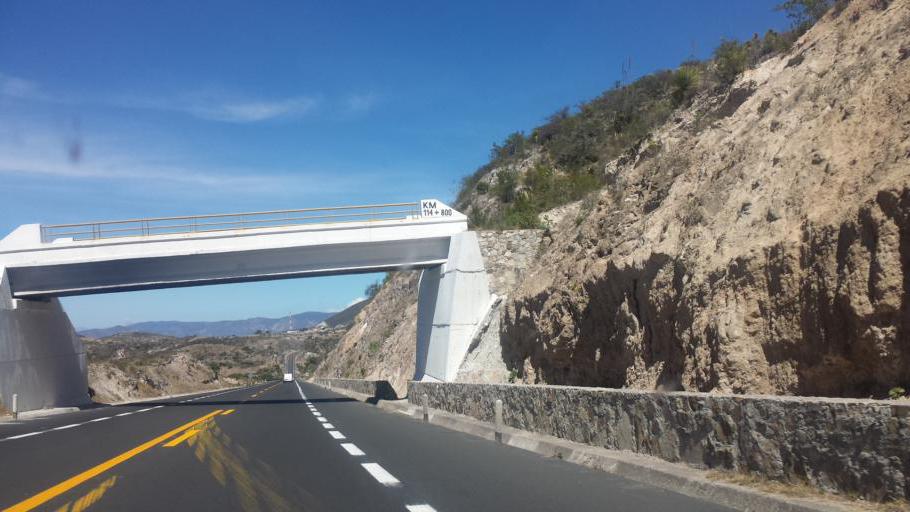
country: MX
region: Oaxaca
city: San Gabriel Casa Blanca
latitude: 17.9635
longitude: -97.3575
